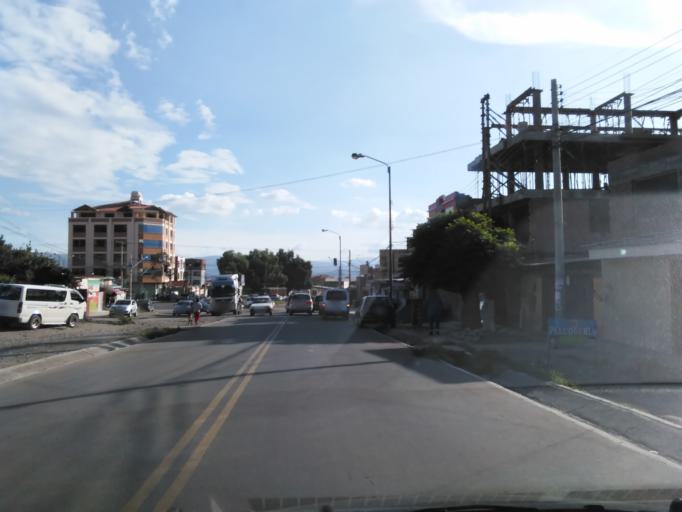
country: BO
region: Cochabamba
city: Cochabamba
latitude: -17.3537
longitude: -66.1872
